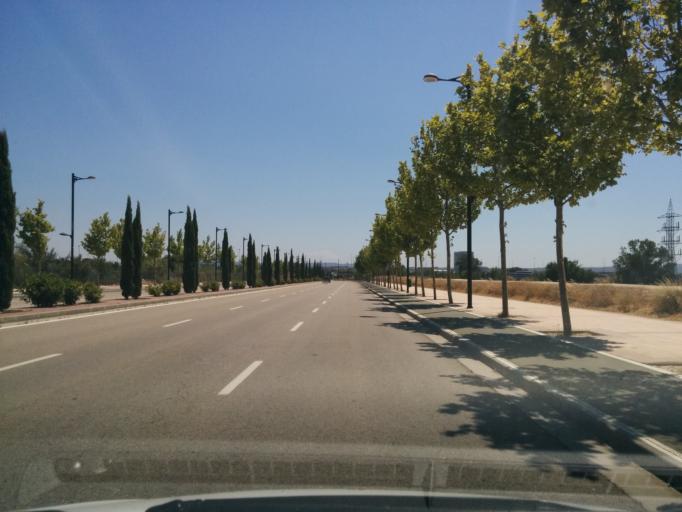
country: ES
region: Aragon
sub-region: Provincia de Zaragoza
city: Almozara
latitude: 41.6844
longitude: -0.8975
